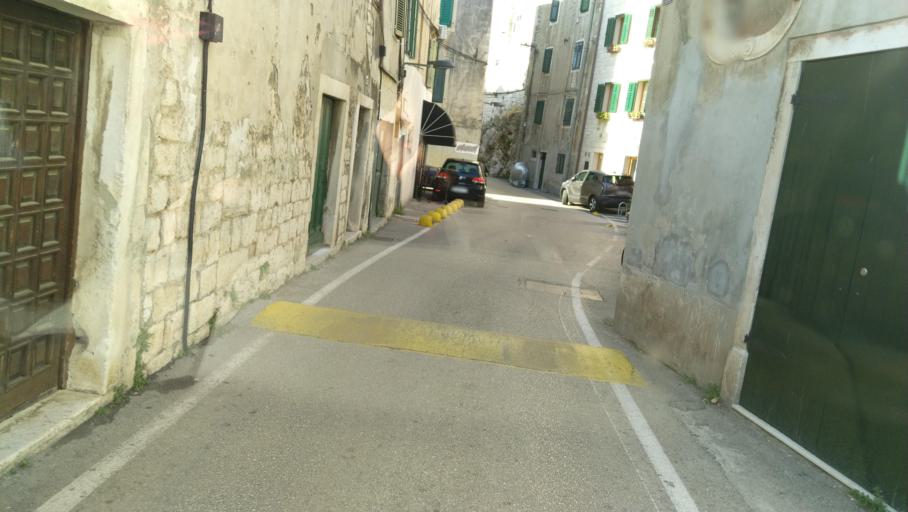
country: HR
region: Sibensko-Kniniska
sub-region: Grad Sibenik
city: Sibenik
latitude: 43.7372
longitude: 15.8879
